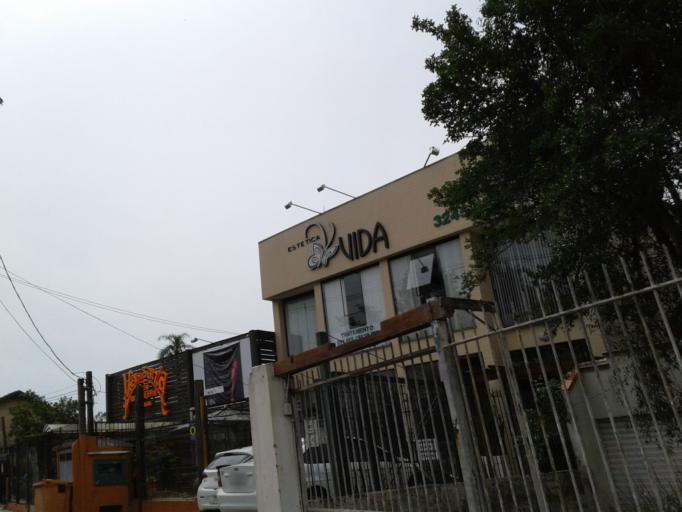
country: BR
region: Rio Grande do Sul
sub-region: Porto Alegre
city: Porto Alegre
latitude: -30.1360
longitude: -51.2225
